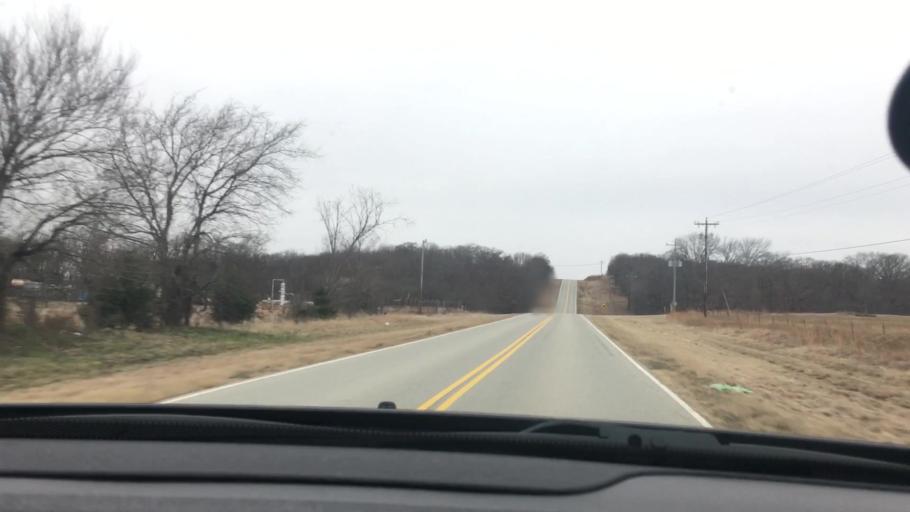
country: US
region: Oklahoma
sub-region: Coal County
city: Coalgate
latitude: 34.5057
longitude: -96.3128
